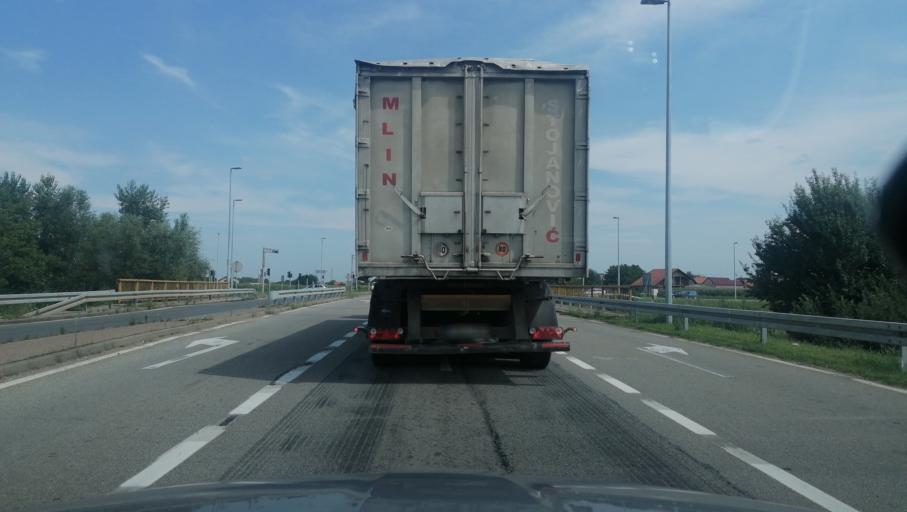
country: BA
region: Republika Srpska
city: Bijeljina
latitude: 44.7741
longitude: 19.1999
